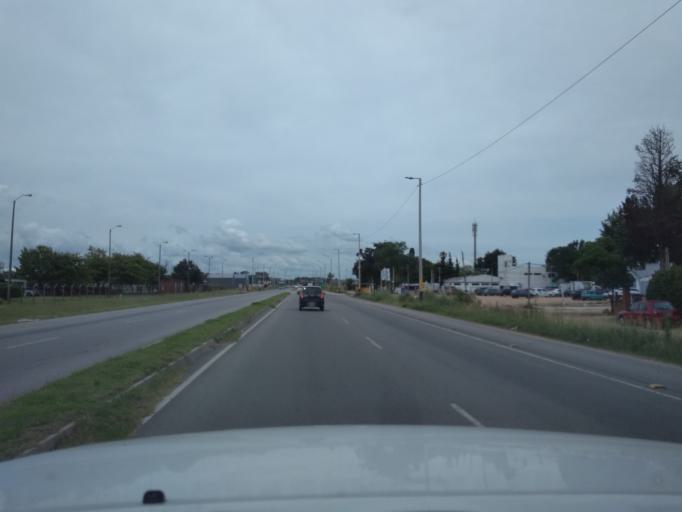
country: UY
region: Canelones
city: Paso de Carrasco
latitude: -34.8473
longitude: -56.0292
